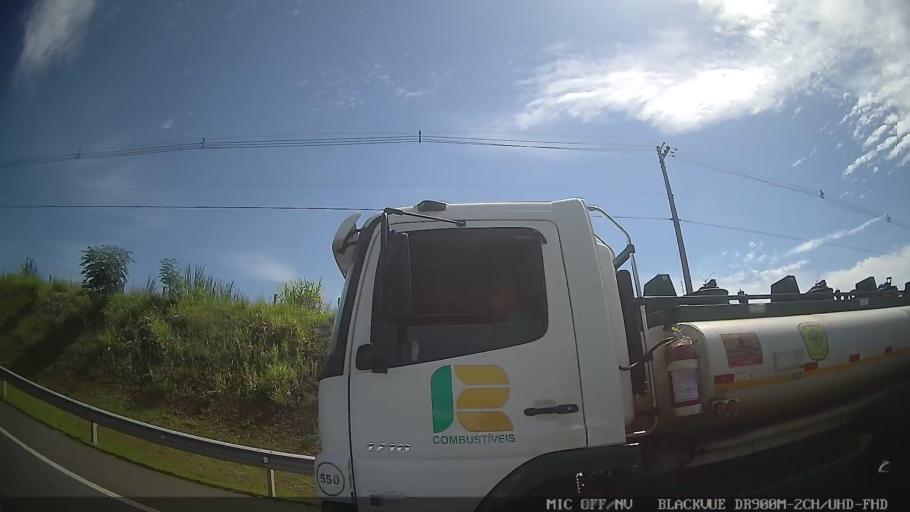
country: BR
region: Sao Paulo
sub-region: Porto Feliz
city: Porto Feliz
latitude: -23.1998
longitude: -47.6069
